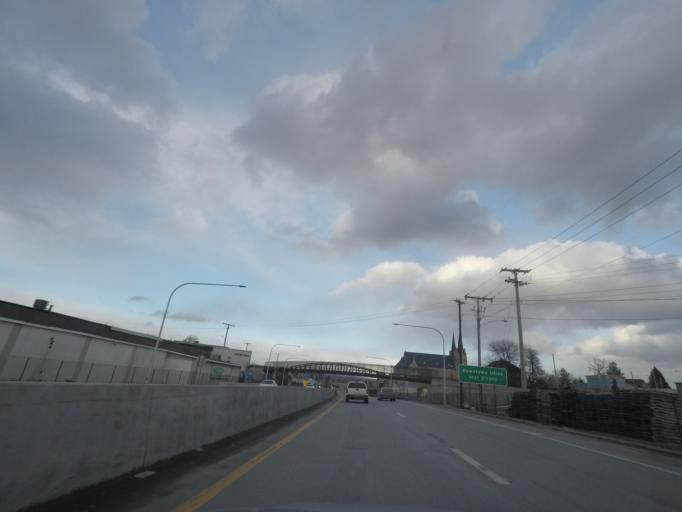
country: US
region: New York
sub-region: Oneida County
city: Utica
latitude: 43.0988
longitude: -75.2477
